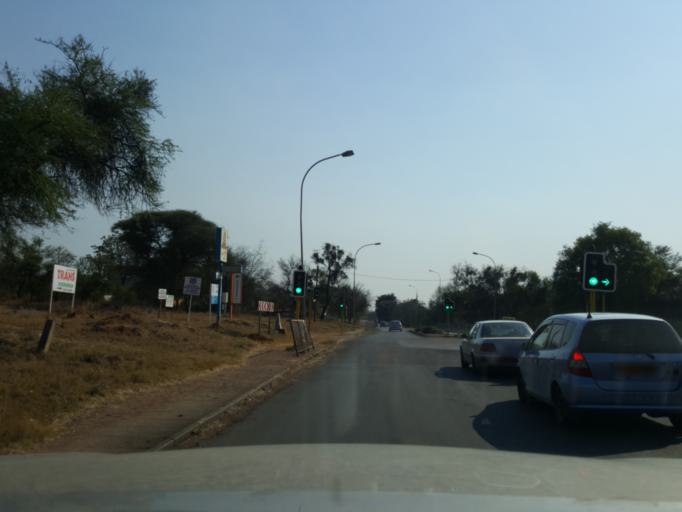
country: BW
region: South East
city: Lobatse
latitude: -25.2260
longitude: 25.6767
